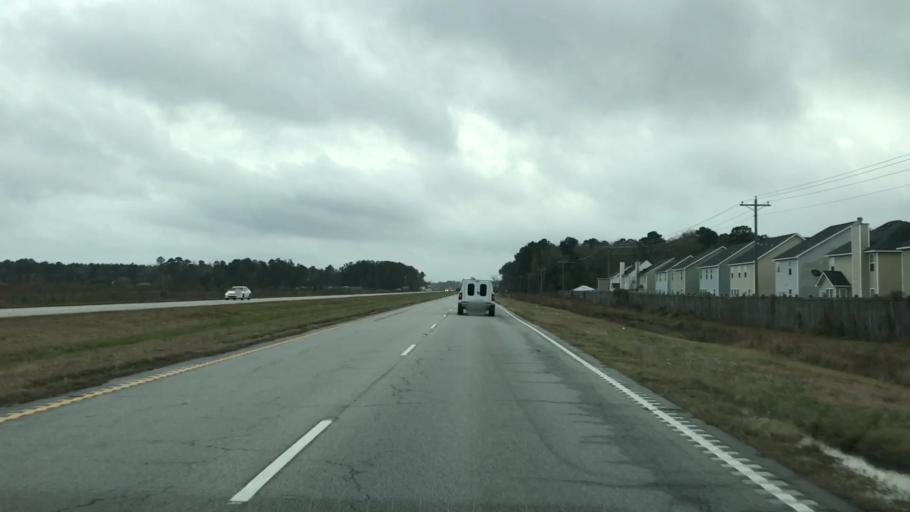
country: US
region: South Carolina
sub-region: Berkeley County
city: Moncks Corner
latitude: 33.1532
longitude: -80.0330
